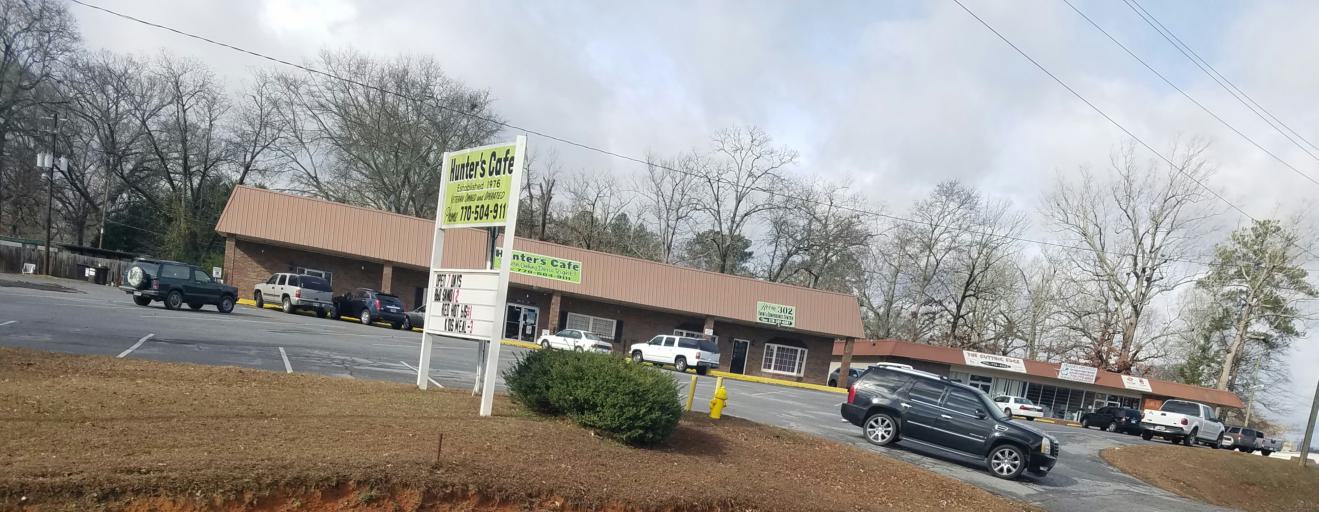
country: US
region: Georgia
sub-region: Butts County
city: Jackson
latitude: 33.2917
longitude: -83.9516
